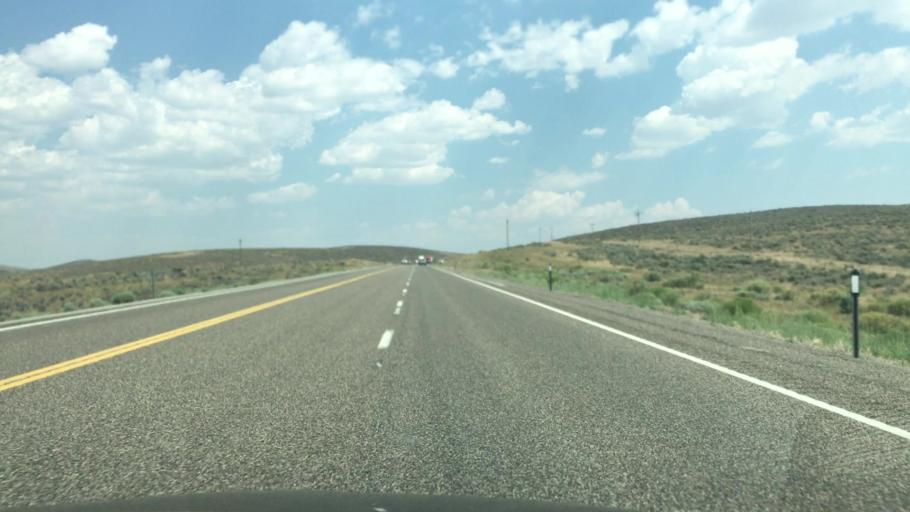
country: US
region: Nevada
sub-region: Elko County
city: Wells
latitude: 41.1815
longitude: -114.8761
